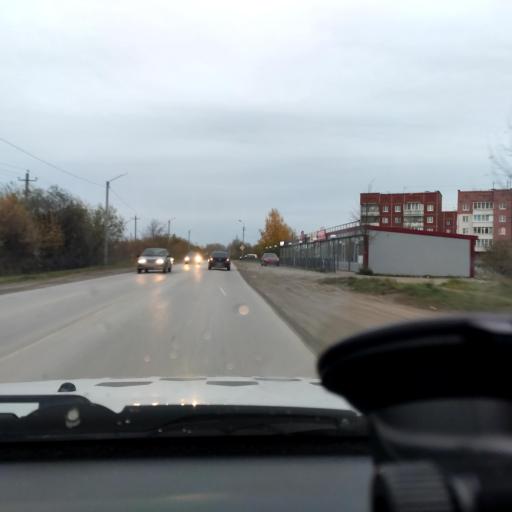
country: RU
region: Perm
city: Kondratovo
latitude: 57.9750
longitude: 56.1105
